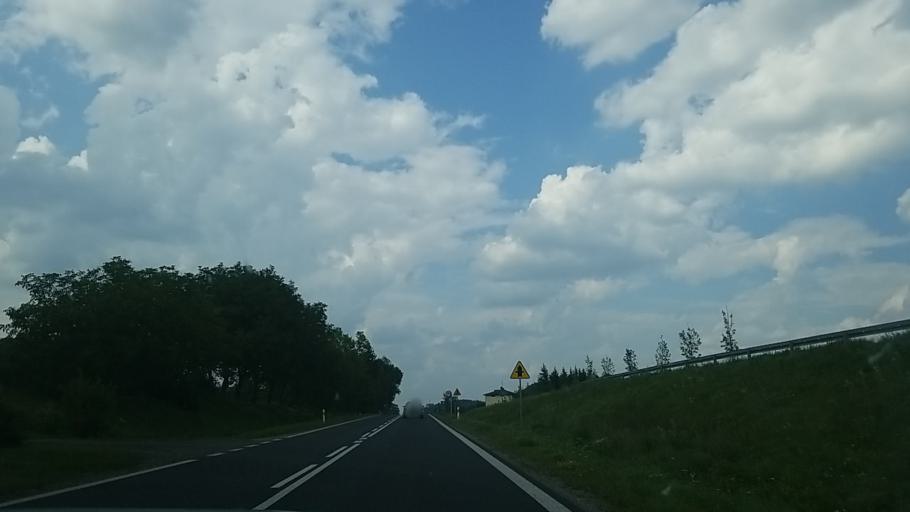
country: PL
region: Lublin Voivodeship
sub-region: Powiat bilgorajski
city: Goraj
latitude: 50.7359
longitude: 22.6682
